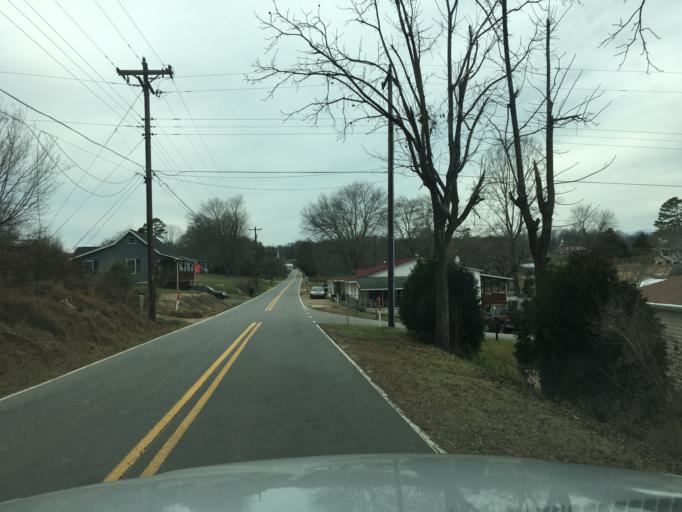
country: US
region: North Carolina
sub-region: McDowell County
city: West Marion
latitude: 35.6150
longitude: -81.9761
